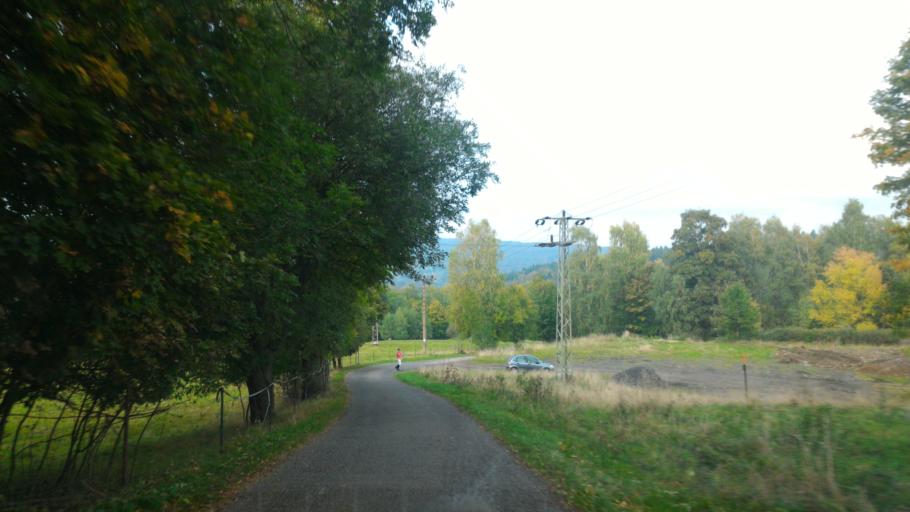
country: CZ
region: Ustecky
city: Dolni Podluzi
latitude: 50.8635
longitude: 14.5776
